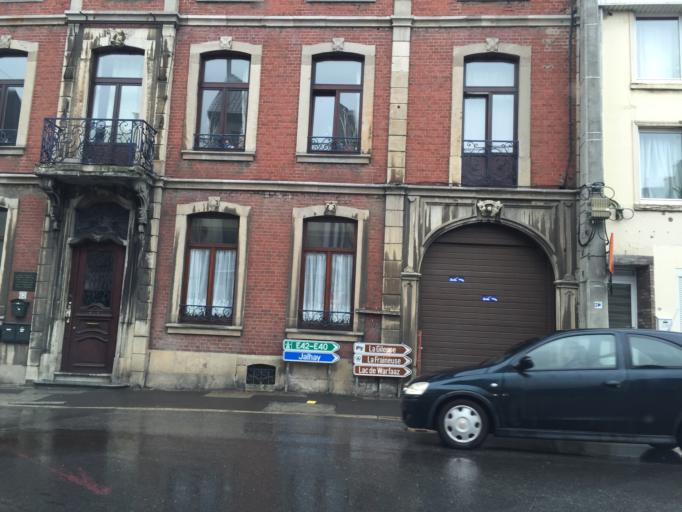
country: BE
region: Wallonia
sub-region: Province de Liege
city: Spa
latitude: 50.4921
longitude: 5.8688
